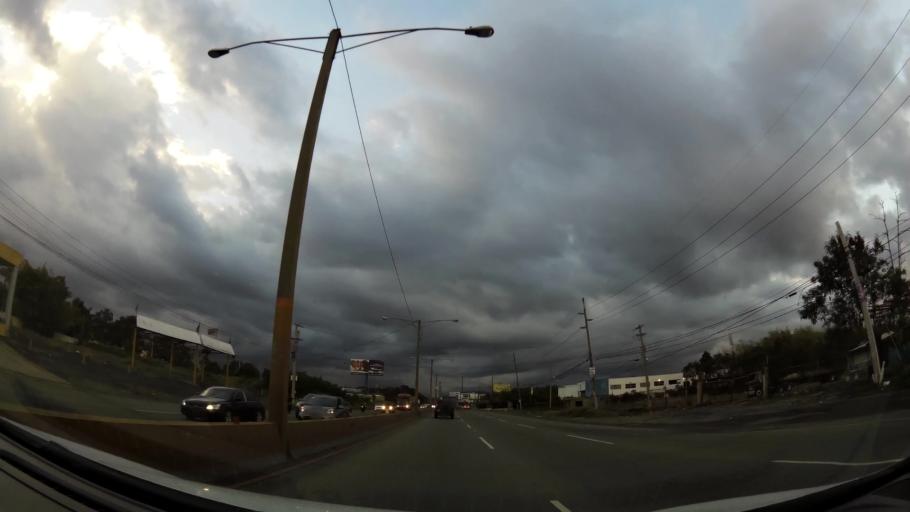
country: DO
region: Santo Domingo
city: Santo Domingo Oeste
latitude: 18.5544
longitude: -70.0562
